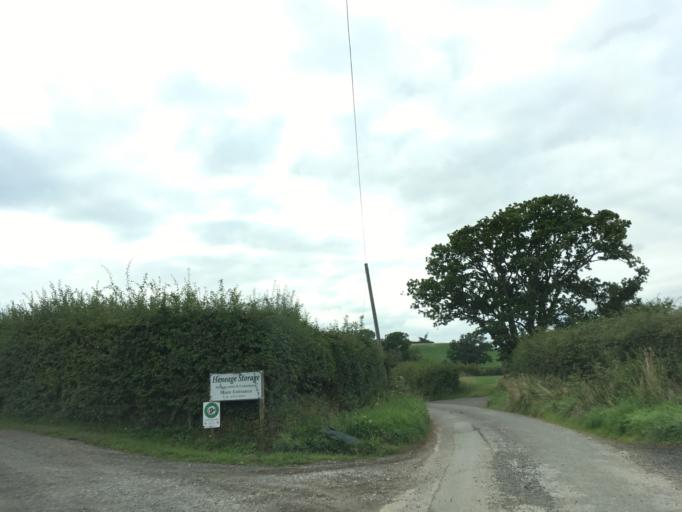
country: GB
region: England
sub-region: South Gloucestershire
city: Falfield
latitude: 51.6414
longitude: -2.4590
